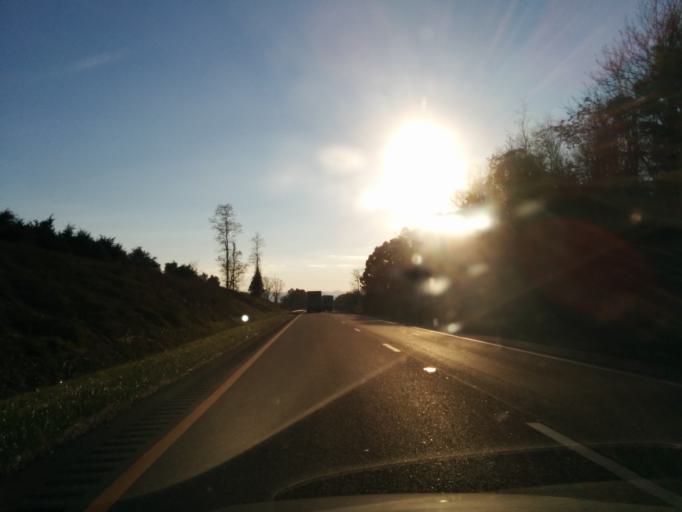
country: US
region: Virginia
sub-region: Rockbridge County
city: East Lexington
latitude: 37.8625
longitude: -79.3417
